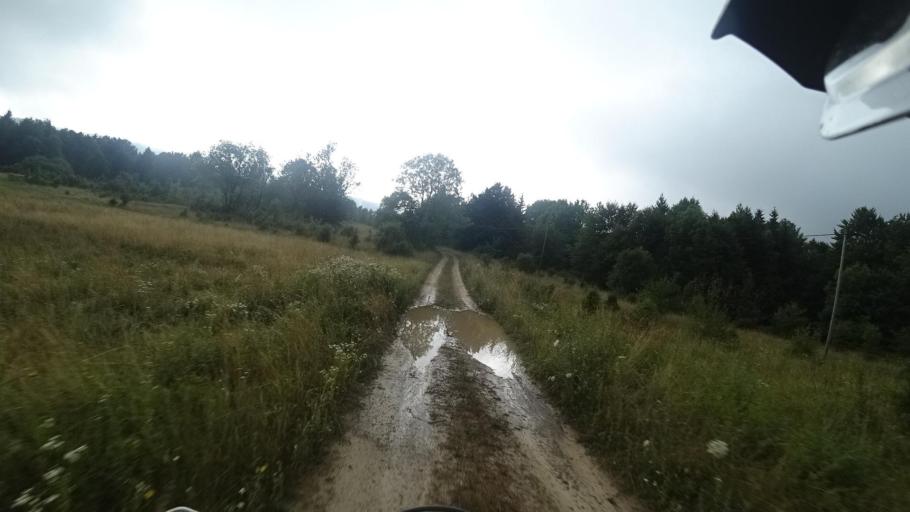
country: HR
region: Licko-Senjska
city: Jezerce
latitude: 44.8203
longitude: 15.6217
